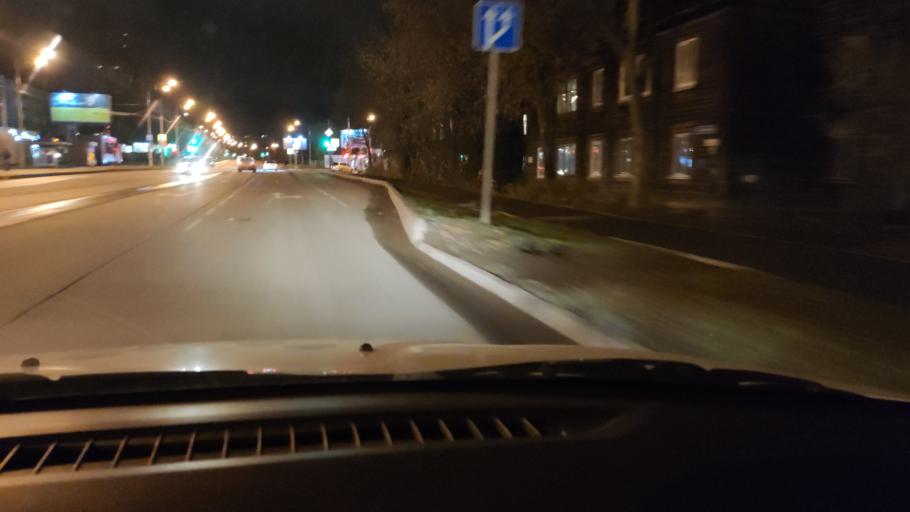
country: RU
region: Perm
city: Perm
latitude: 57.9785
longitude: 56.2155
